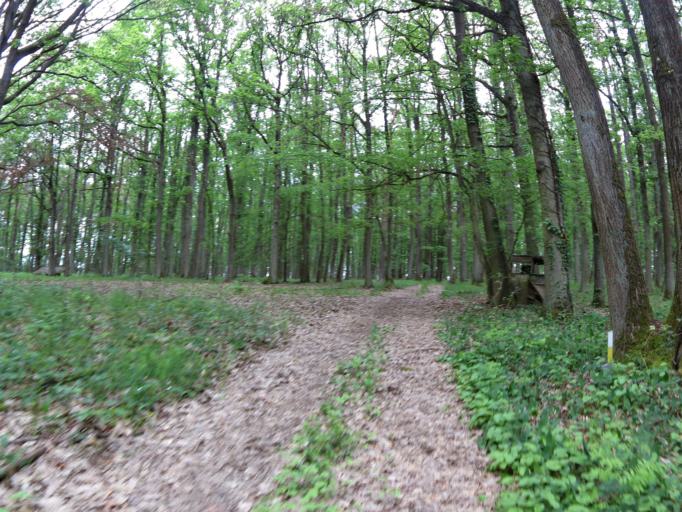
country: DE
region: Bavaria
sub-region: Regierungsbezirk Unterfranken
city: Sommerhausen
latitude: 49.7150
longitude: 10.0303
